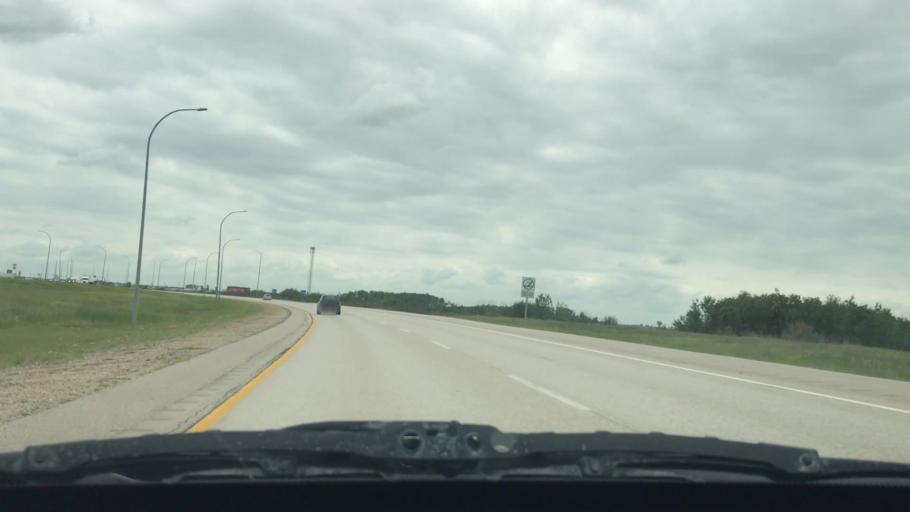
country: CA
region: Manitoba
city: Winnipeg
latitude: 49.8256
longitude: -96.9474
